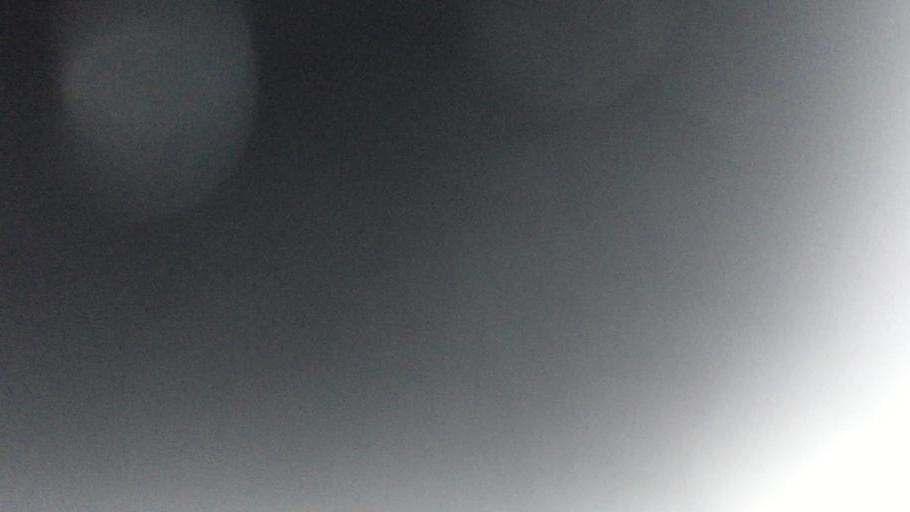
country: US
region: Maryland
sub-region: Frederick County
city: Clover Hill
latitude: 39.4478
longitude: -77.4108
